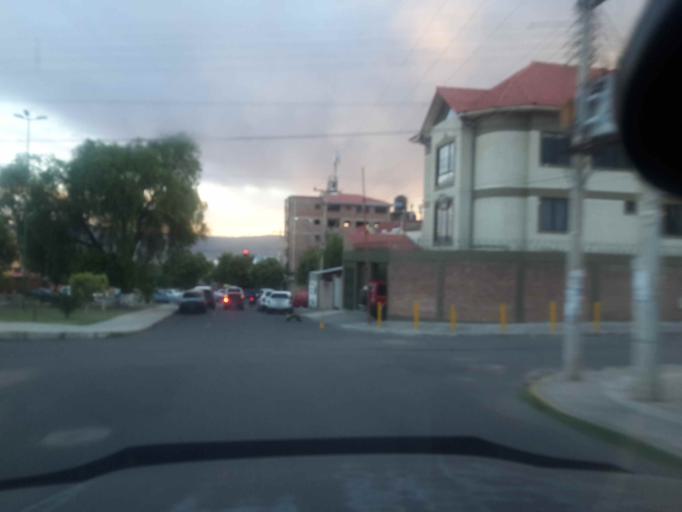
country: BO
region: Cochabamba
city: Cochabamba
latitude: -17.3598
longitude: -66.1701
